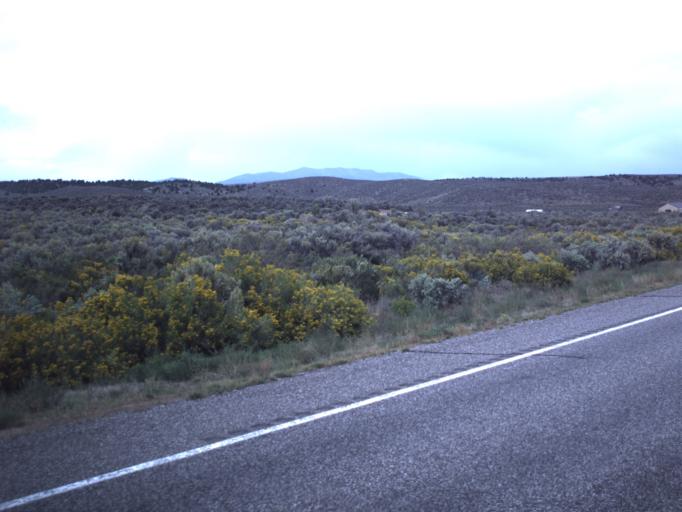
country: US
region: Utah
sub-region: Garfield County
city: Panguitch
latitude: 38.0015
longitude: -112.3839
